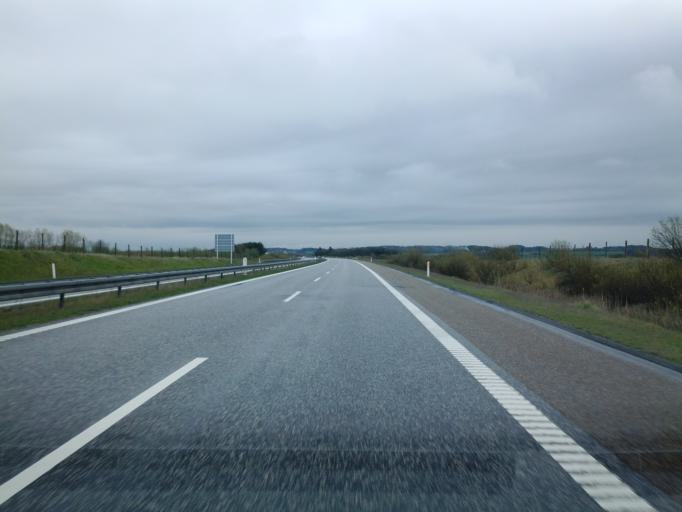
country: DK
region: North Denmark
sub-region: Bronderslev Kommune
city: Dronninglund
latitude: 57.2584
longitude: 10.3564
